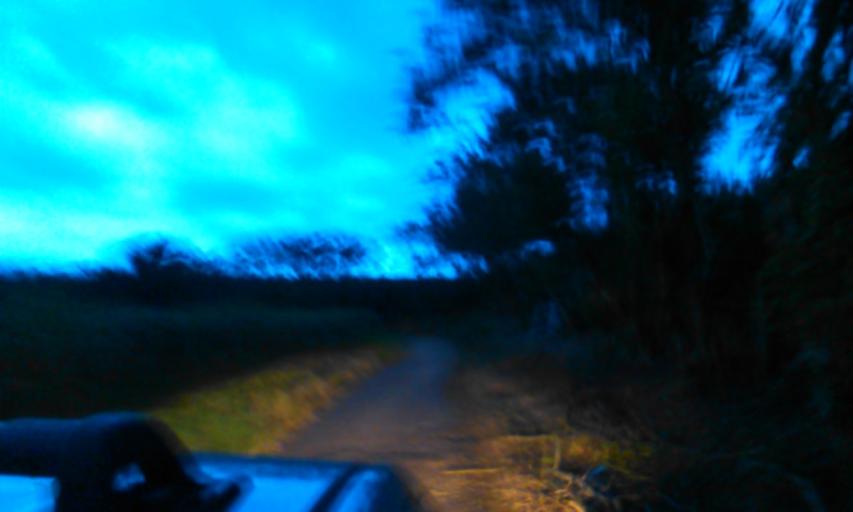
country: CO
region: Quindio
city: La Tebaida
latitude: 4.4955
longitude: -75.8570
